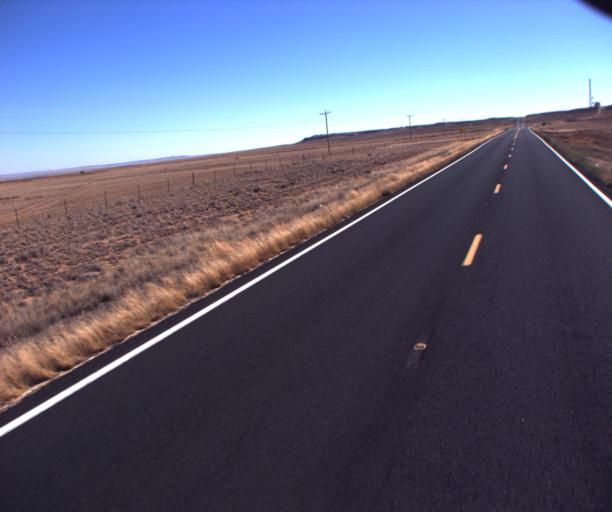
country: US
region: Arizona
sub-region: Coconino County
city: Tuba City
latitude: 36.0000
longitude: -111.0355
